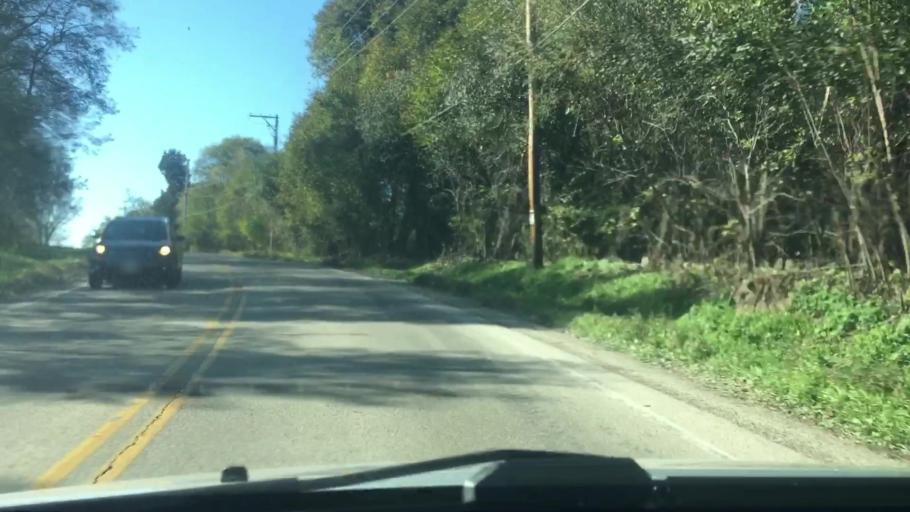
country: US
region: Wisconsin
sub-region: Waukesha County
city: Wales
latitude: 42.9920
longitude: -88.3737
